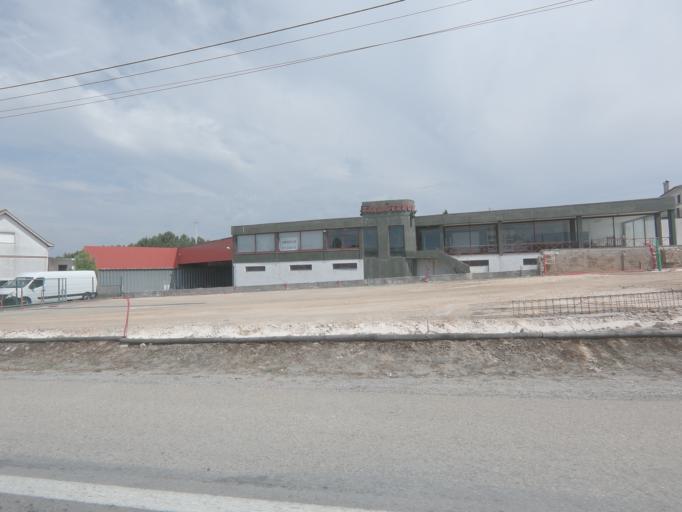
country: PT
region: Leiria
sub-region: Leiria
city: Caranguejeira
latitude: 39.8269
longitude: -8.7233
